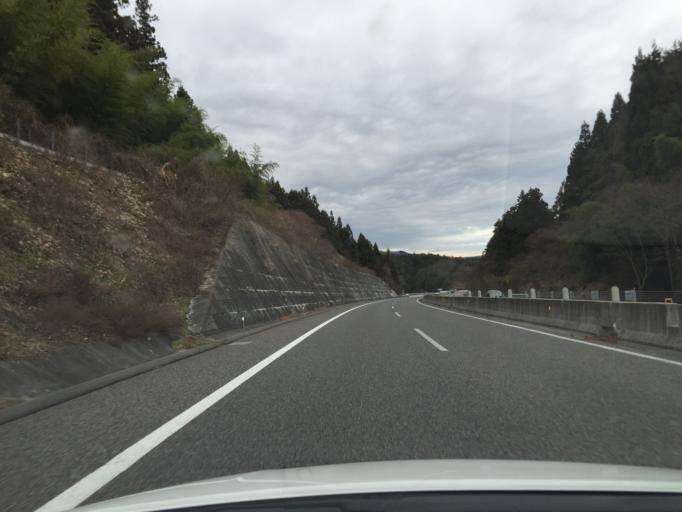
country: JP
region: Fukushima
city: Funehikimachi-funehiki
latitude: 37.3095
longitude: 140.6102
